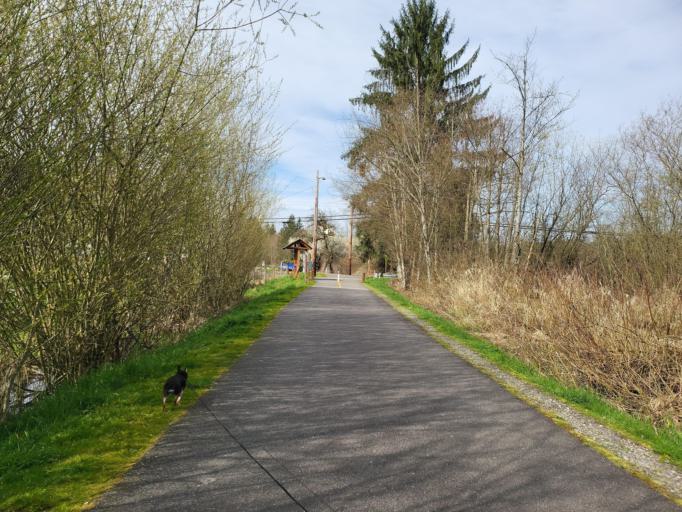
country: US
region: Washington
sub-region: King County
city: East Hill-Meridian
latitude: 47.4155
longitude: -122.1587
